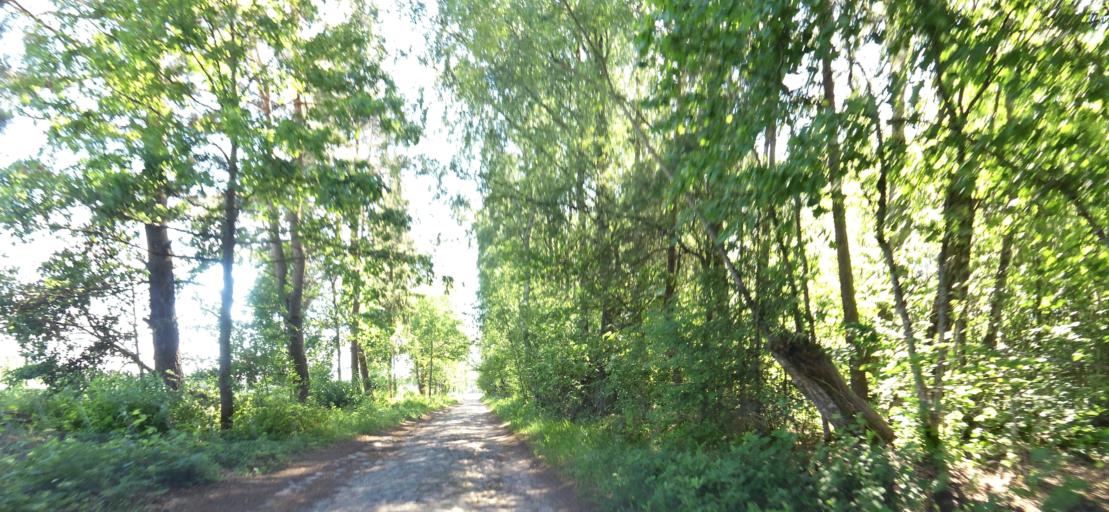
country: LT
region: Vilnius County
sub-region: Vilnius
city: Fabijoniskes
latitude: 54.8385
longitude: 25.3260
